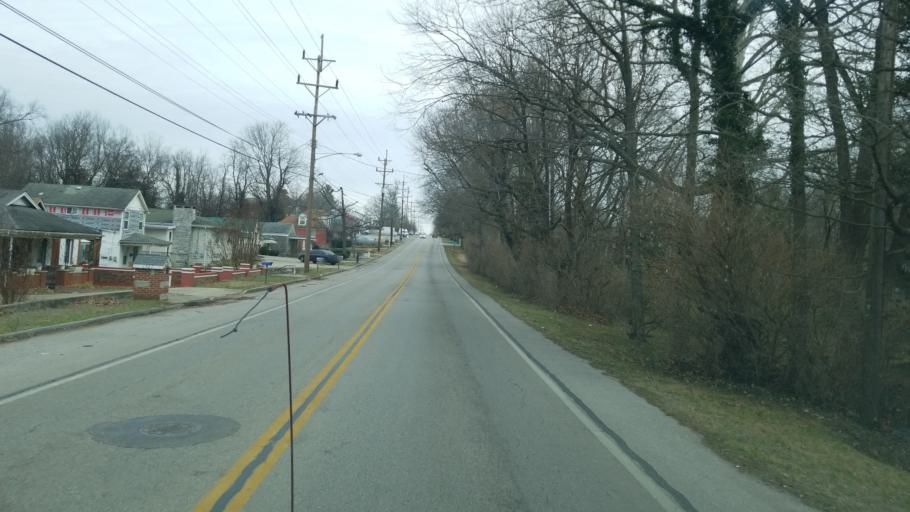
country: US
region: Kentucky
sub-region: Fayette County
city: Lexington-Fayette
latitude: 38.0692
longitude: -84.4645
